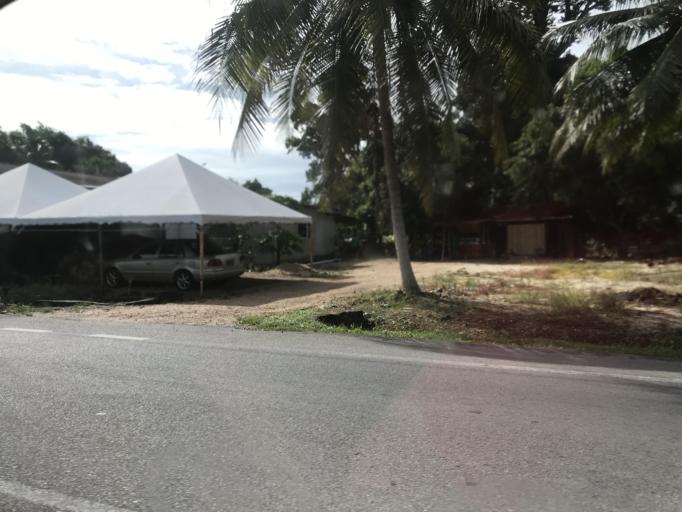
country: MY
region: Kelantan
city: Kota Bharu
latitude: 6.1312
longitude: 102.1763
